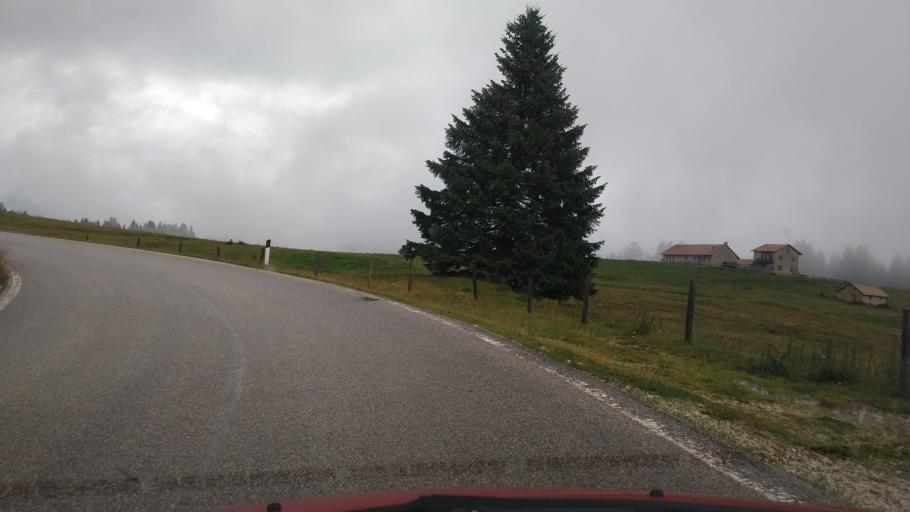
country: IT
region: Veneto
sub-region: Provincia di Vicenza
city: Lastebasse
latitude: 45.9045
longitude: 11.2482
